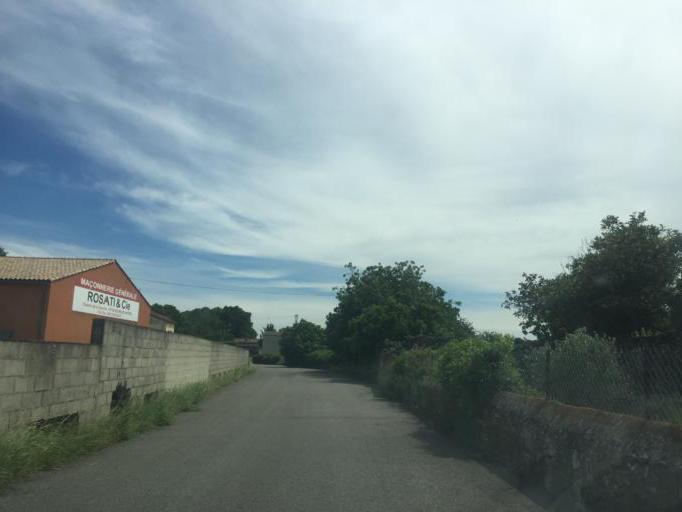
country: FR
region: Rhone-Alpes
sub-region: Departement de l'Ardeche
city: Bourg-Saint-Andeol
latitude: 44.3629
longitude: 4.6462
